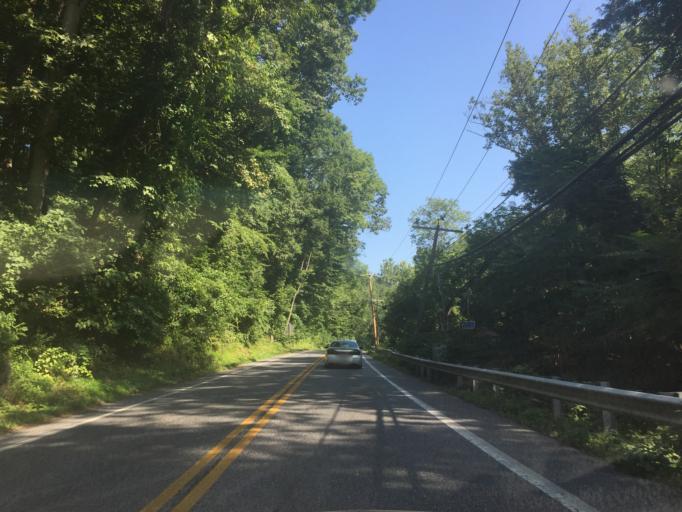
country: US
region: Maryland
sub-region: Baltimore County
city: Mays Chapel
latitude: 39.3913
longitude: -76.6609
